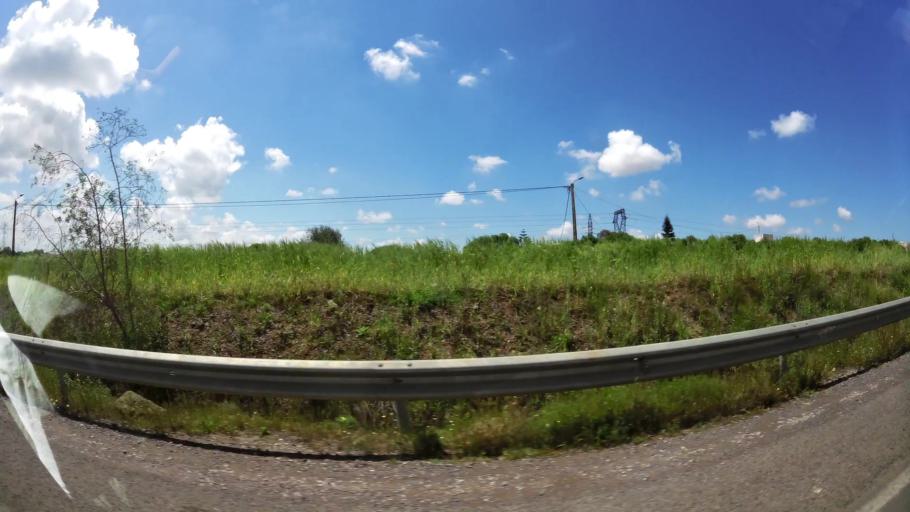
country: MA
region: Grand Casablanca
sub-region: Casablanca
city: Casablanca
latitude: 33.5179
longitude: -7.6152
